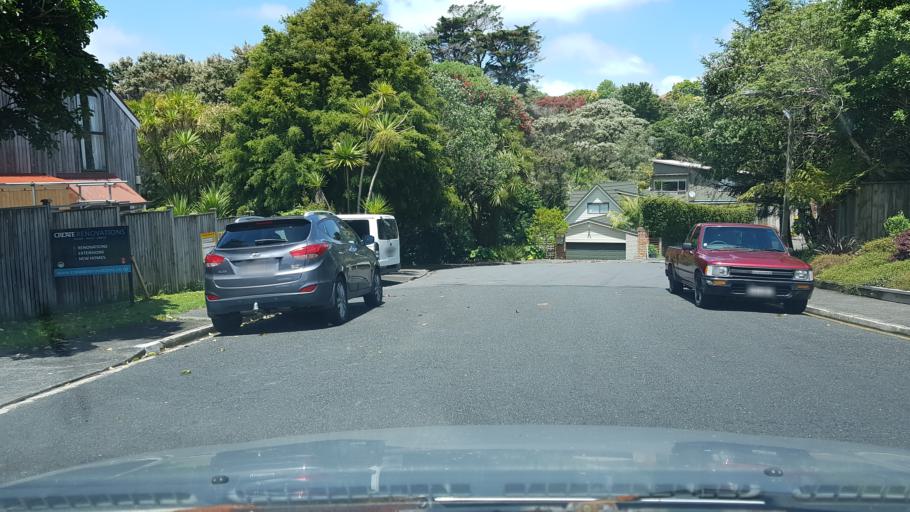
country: NZ
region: Auckland
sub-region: Auckland
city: North Shore
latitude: -36.8080
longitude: 174.7168
